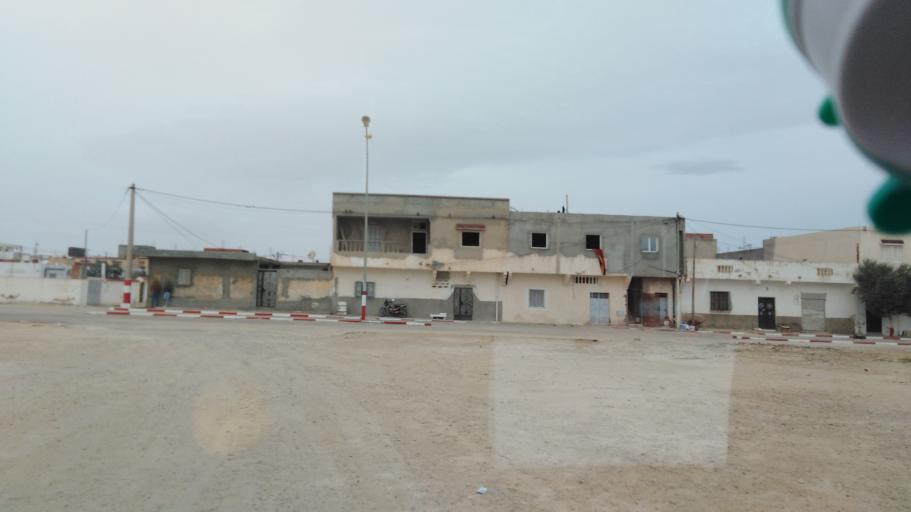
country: TN
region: Qabis
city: Gabes
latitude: 33.9494
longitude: 10.0038
